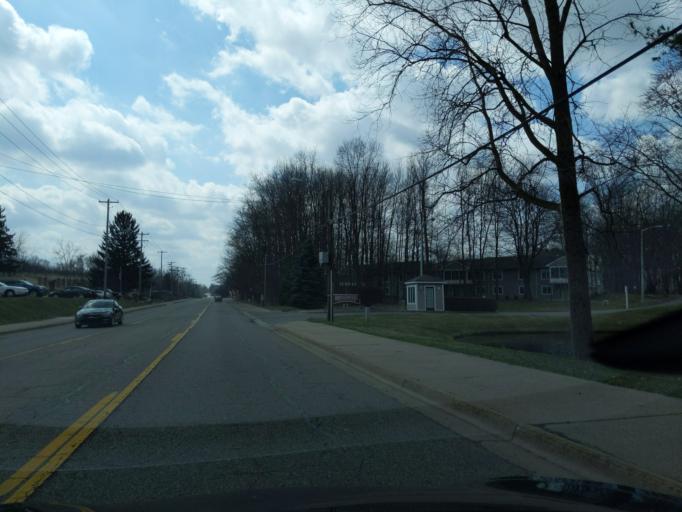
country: US
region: Michigan
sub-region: Calhoun County
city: Lakeview
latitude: 42.2553
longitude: -85.1987
